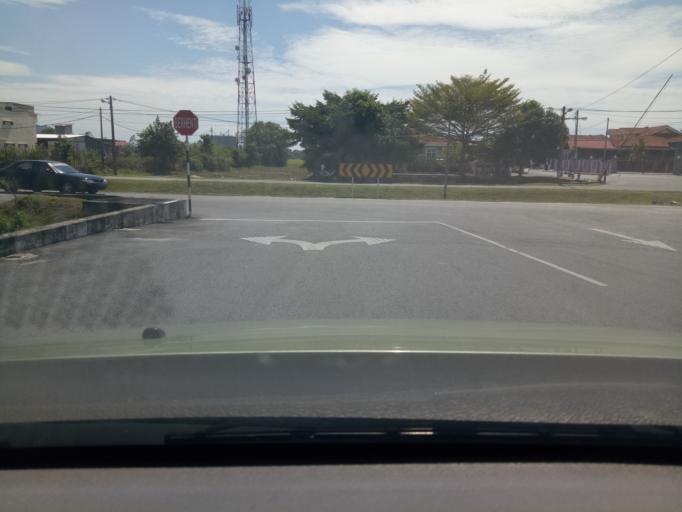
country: MY
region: Kedah
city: Gurun
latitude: 5.8584
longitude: 100.4522
